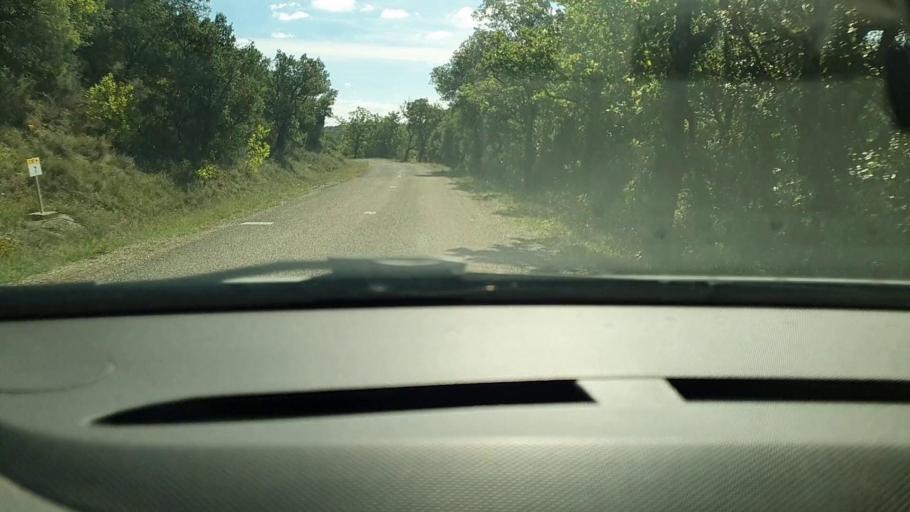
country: FR
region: Languedoc-Roussillon
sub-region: Departement du Gard
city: Barjac
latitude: 44.1974
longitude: 4.3130
